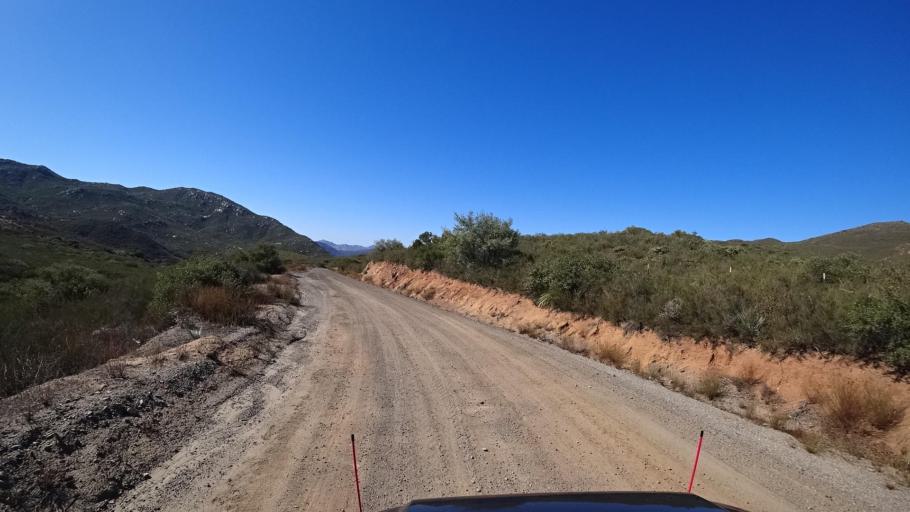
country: US
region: California
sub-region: San Diego County
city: Descanso
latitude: 32.8697
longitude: -116.6587
